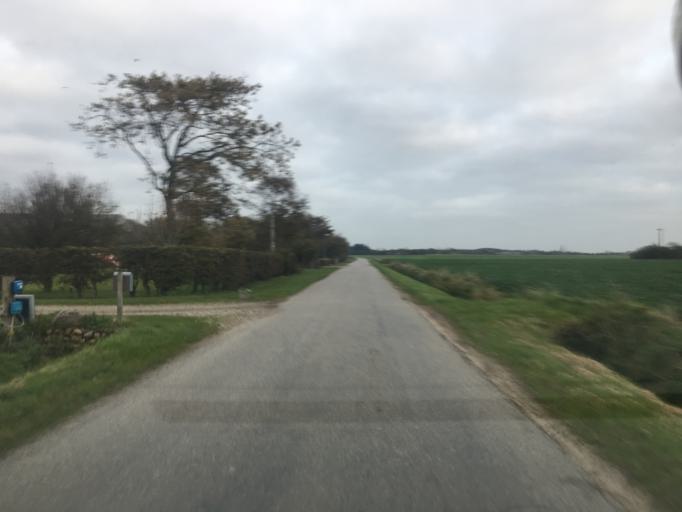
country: DE
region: Schleswig-Holstein
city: Aventoft
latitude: 54.9464
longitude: 8.7759
